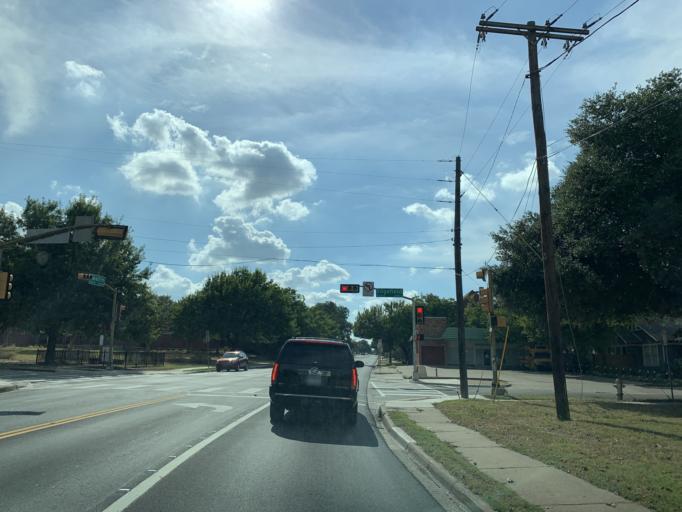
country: US
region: Texas
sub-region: Dallas County
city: Cockrell Hill
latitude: 32.7414
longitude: -96.8439
